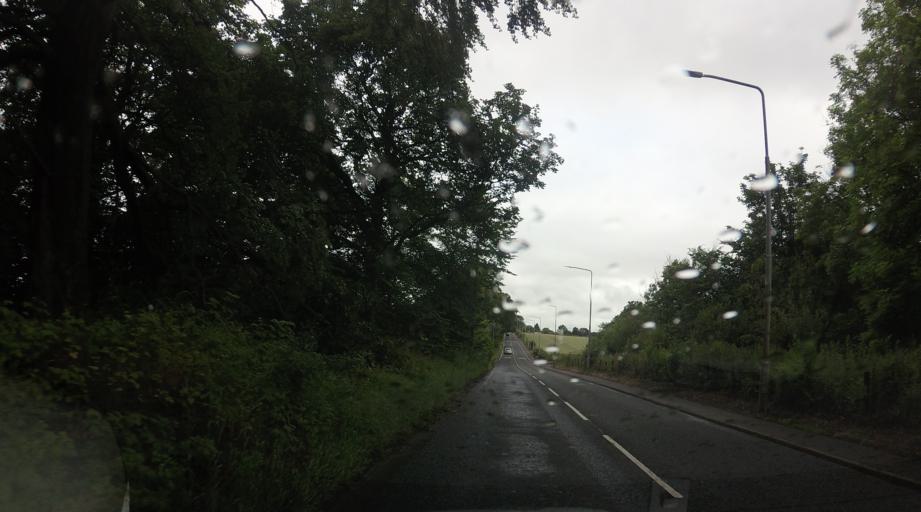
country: GB
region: Scotland
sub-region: West Lothian
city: Livingston
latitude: 55.9208
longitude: -3.5072
